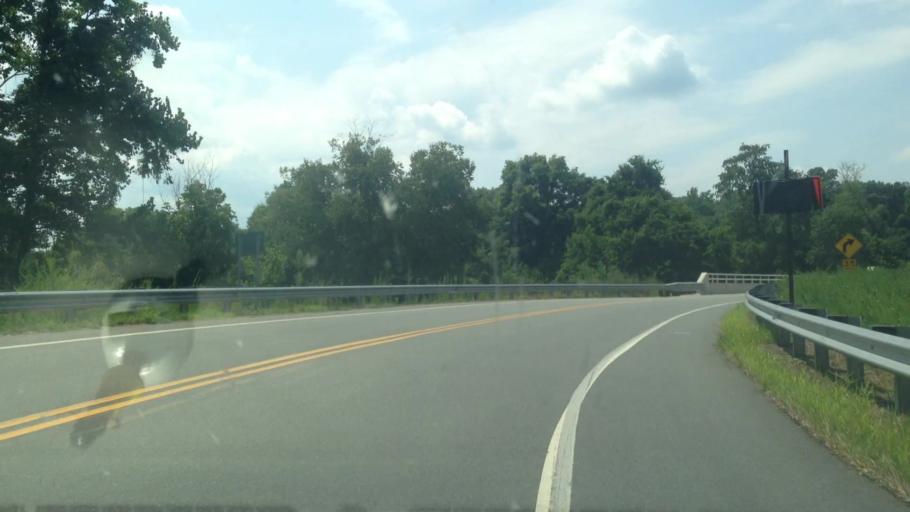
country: US
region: North Carolina
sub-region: Stokes County
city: Walnut Cove
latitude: 36.3183
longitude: -80.0491
